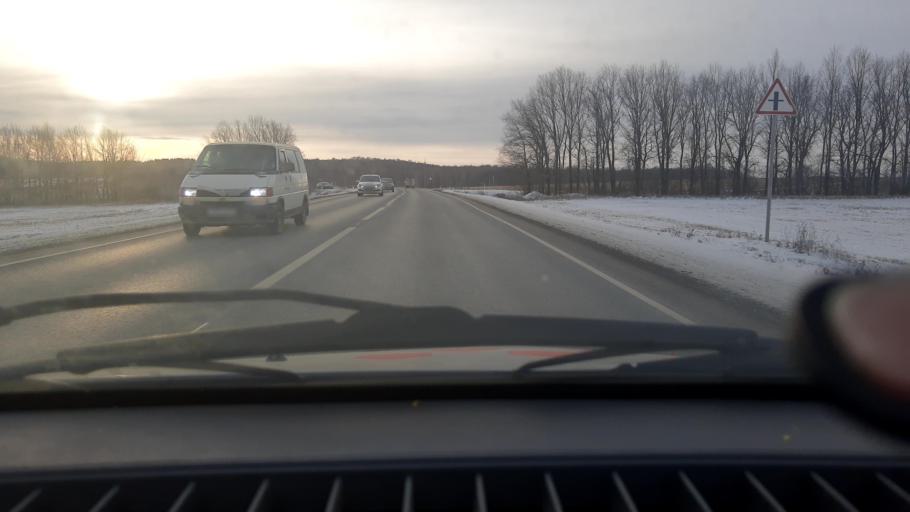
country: RU
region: Bashkortostan
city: Avdon
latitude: 54.8562
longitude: 55.7033
